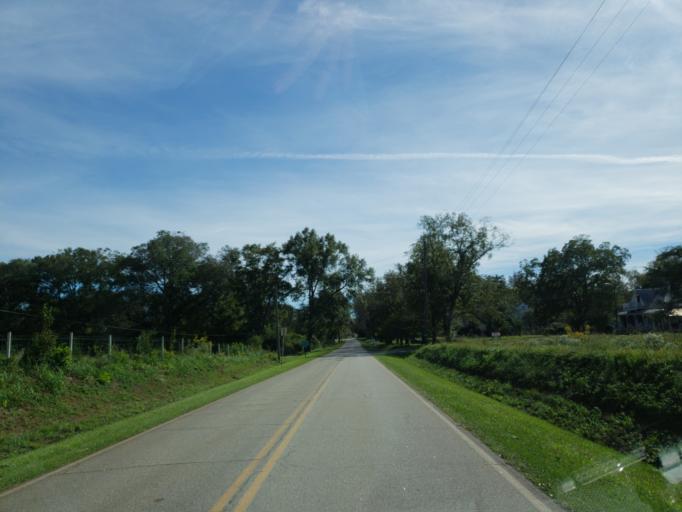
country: US
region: Georgia
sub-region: Crawford County
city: Roberta
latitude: 32.8707
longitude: -84.0921
